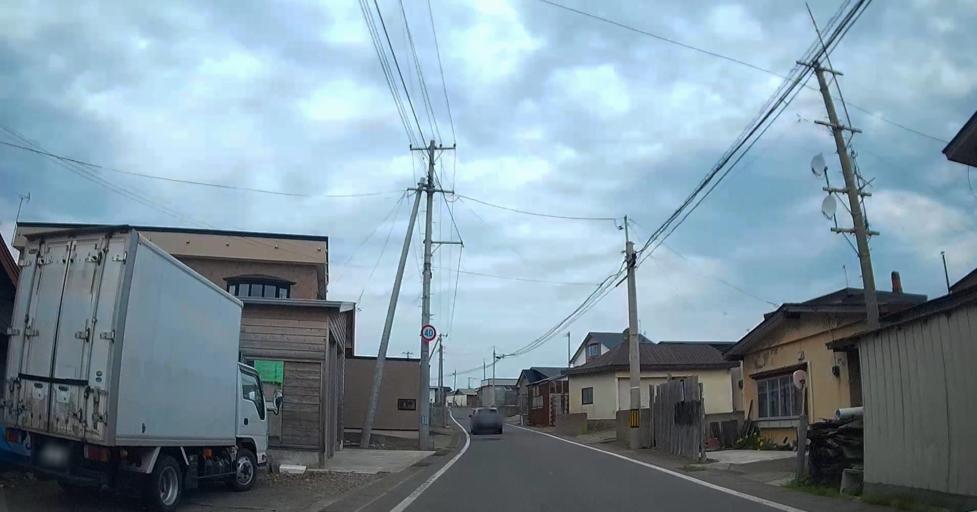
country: JP
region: Aomori
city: Shimokizukuri
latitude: 41.0255
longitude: 140.3275
